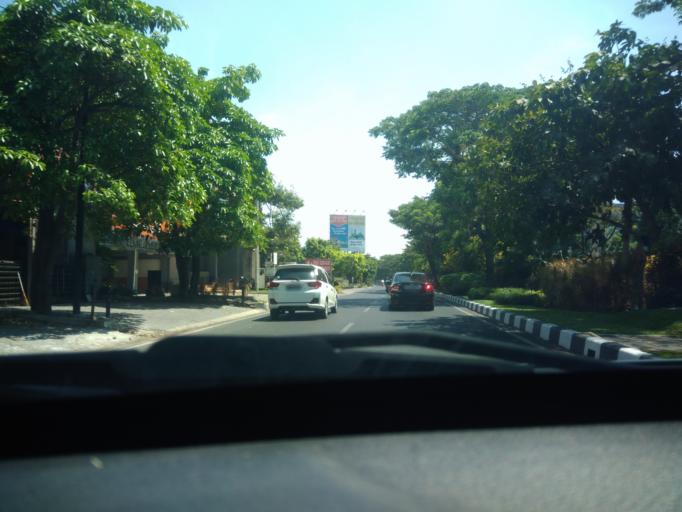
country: ID
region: East Java
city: Semampir
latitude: -7.3065
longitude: 112.7807
